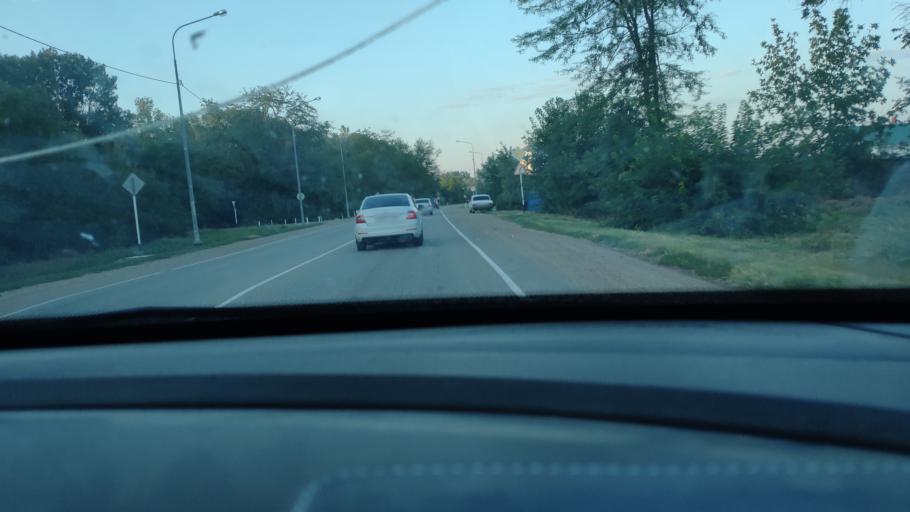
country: RU
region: Krasnodarskiy
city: Novominskaya
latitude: 46.3225
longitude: 38.9342
